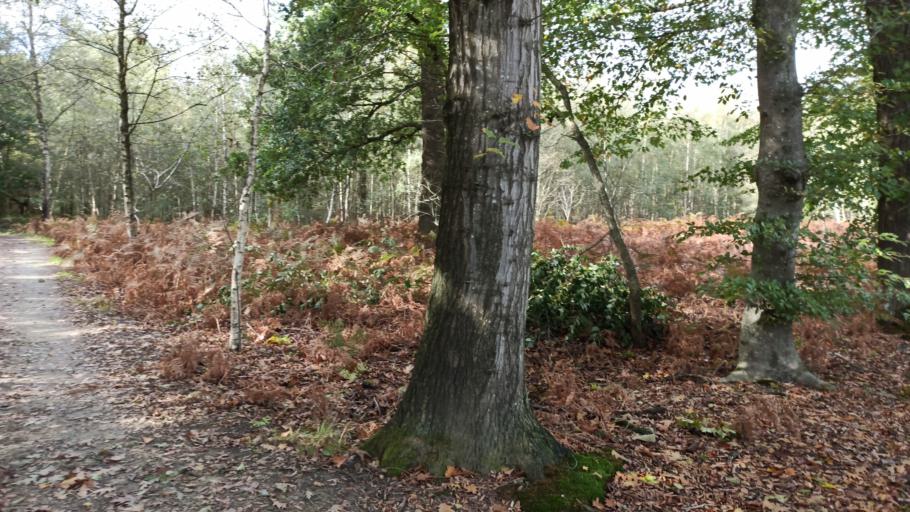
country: BE
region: Flanders
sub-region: Provincie West-Vlaanderen
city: Ruiselede
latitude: 51.0826
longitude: 3.3957
